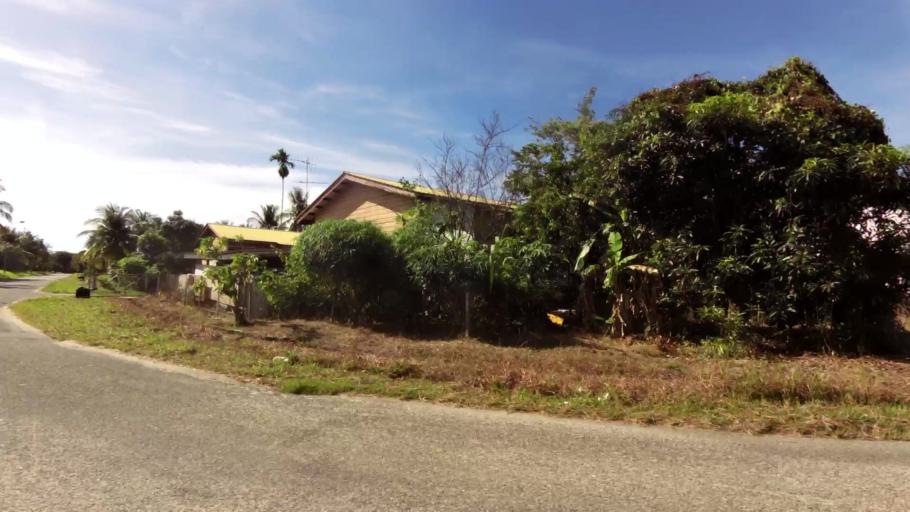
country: BN
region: Belait
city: Kuala Belait
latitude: 4.5792
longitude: 114.2033
